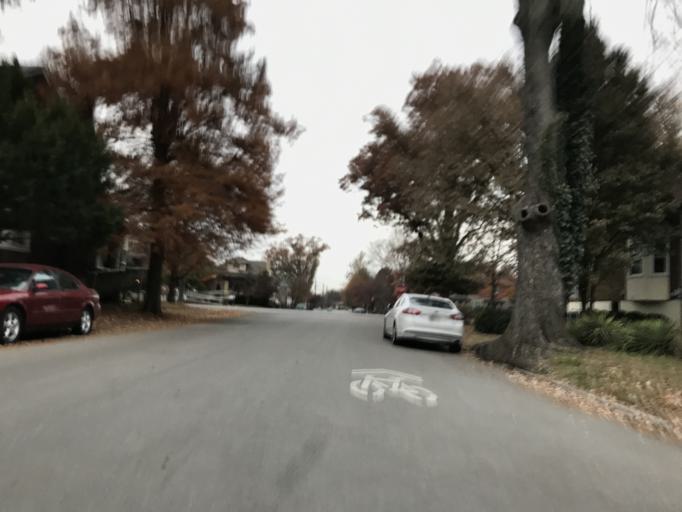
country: US
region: Kentucky
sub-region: Jefferson County
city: Audubon Park
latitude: 38.2167
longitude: -85.7382
